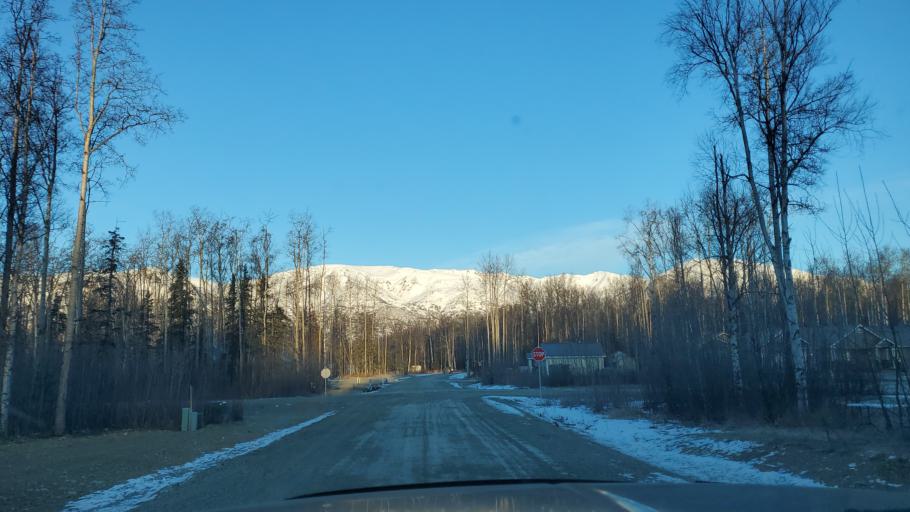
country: US
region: Alaska
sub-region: Matanuska-Susitna Borough
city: Lakes
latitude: 61.6554
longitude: -149.3401
